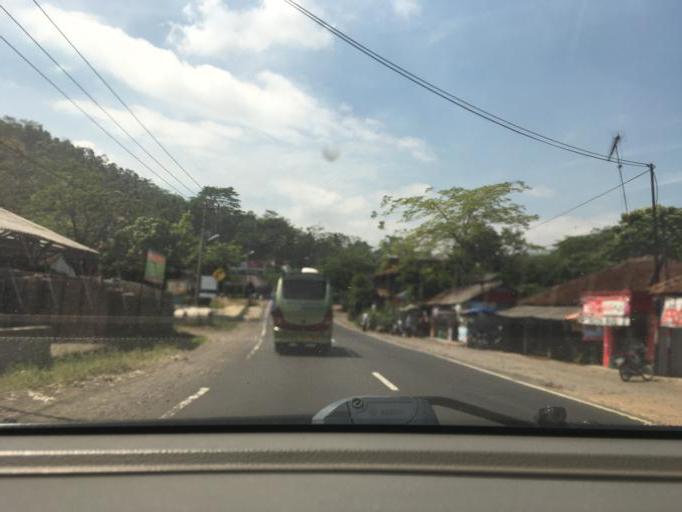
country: ID
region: West Java
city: Tagog
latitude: -7.1170
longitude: 108.1303
